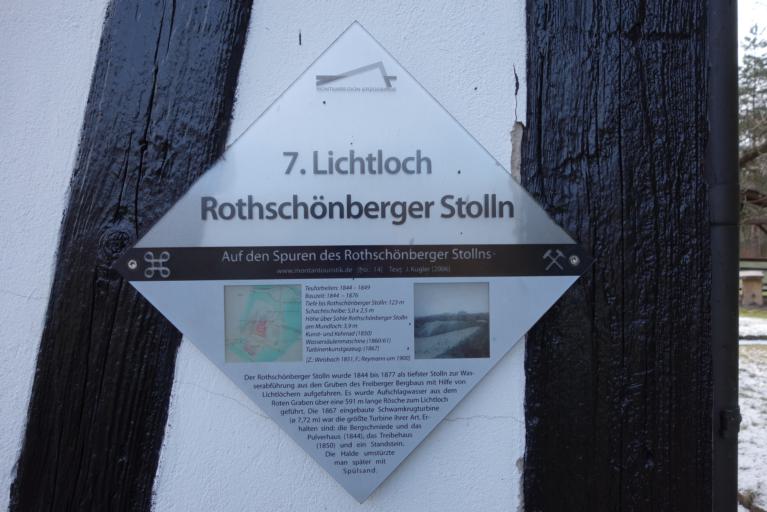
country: DE
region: Saxony
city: Halsbrucke
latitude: 50.9637
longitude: 13.3447
